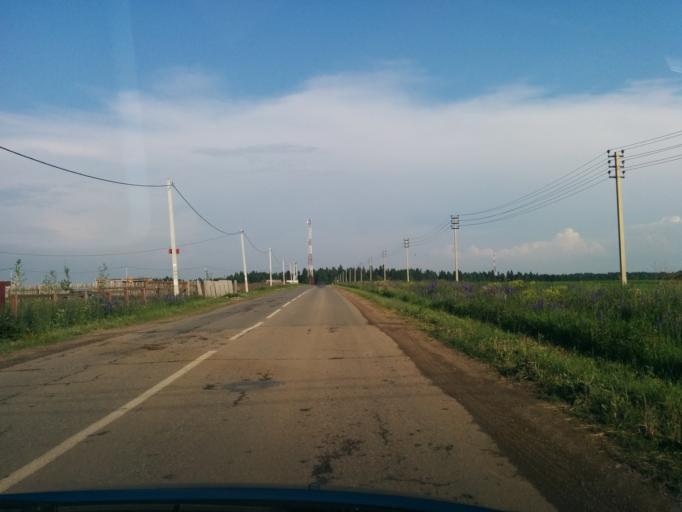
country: RU
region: Perm
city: Polazna
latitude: 58.2402
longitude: 56.2709
